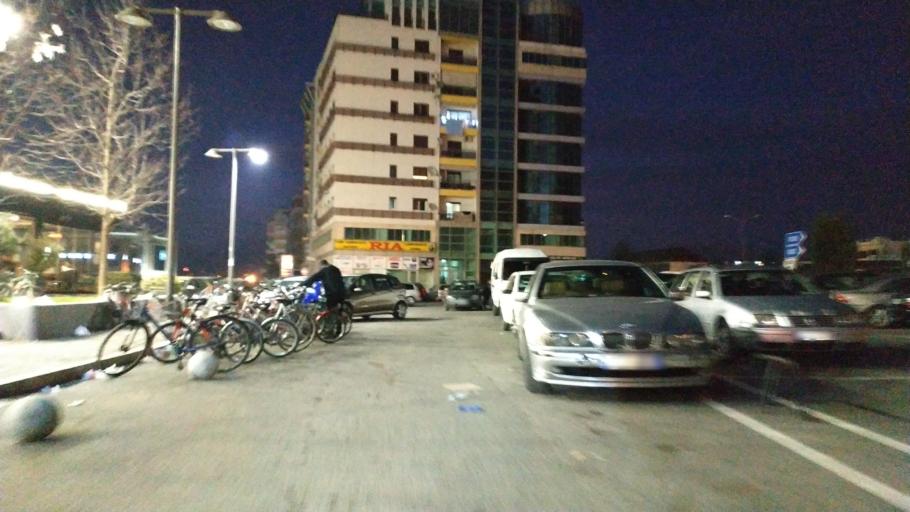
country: AL
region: Shkoder
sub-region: Rrethi i Shkodres
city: Shkoder
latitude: 42.0543
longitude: 19.4983
